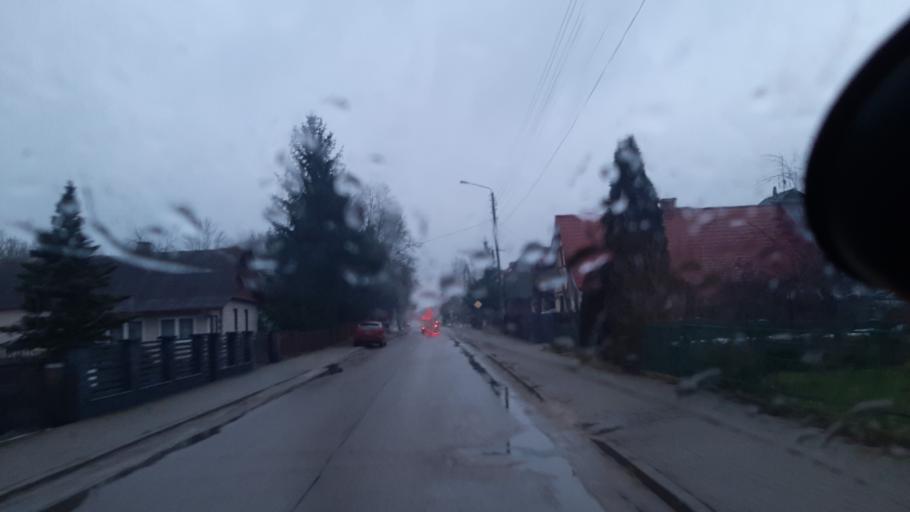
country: PL
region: Lublin Voivodeship
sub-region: Powiat lubartowski
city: Firlej
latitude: 51.5591
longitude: 22.5125
